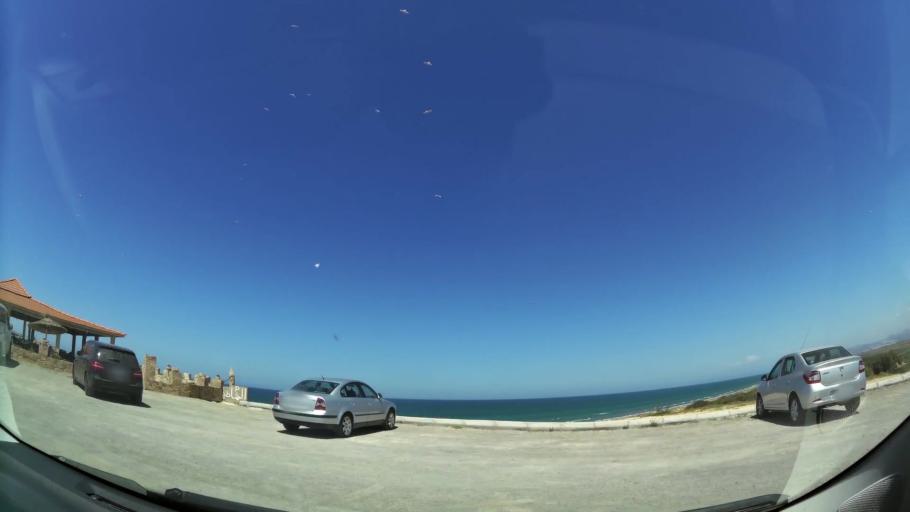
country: MA
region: Oriental
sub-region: Berkane-Taourirt
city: Madagh
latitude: 35.1318
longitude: -2.3971
